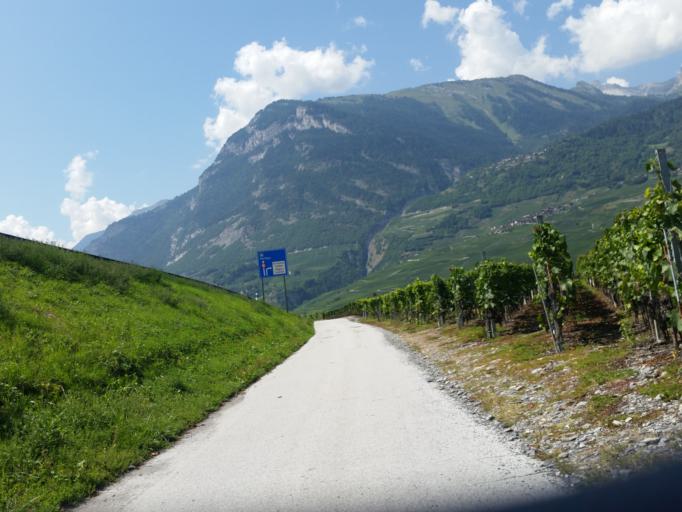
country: CH
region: Valais
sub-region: Martigny District
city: Riddes
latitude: 46.1821
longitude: 7.2206
